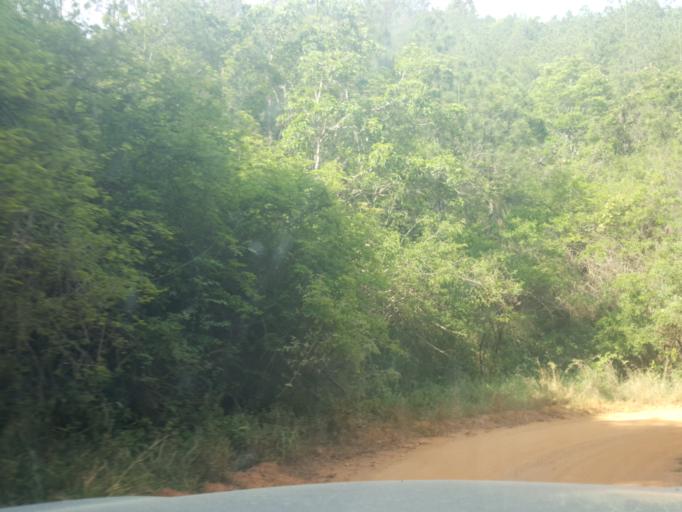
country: ZA
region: Limpopo
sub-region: Mopani District Municipality
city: Hoedspruit
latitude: -24.5919
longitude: 30.8379
